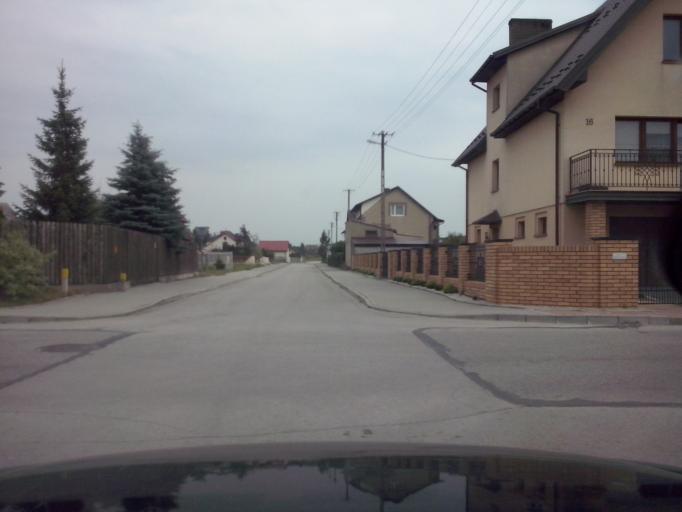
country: PL
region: Swietokrzyskie
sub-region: Powiat kielecki
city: Morawica
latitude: 50.7432
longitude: 20.6268
